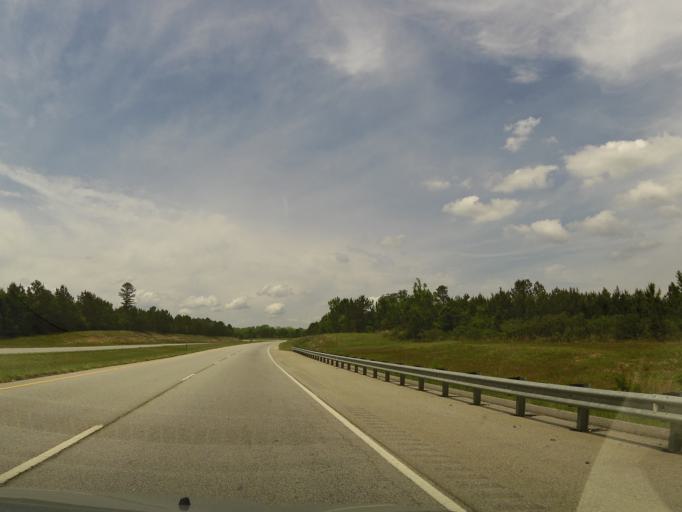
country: US
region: Georgia
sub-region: Emanuel County
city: Swainsboro
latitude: 32.5617
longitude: -82.3407
